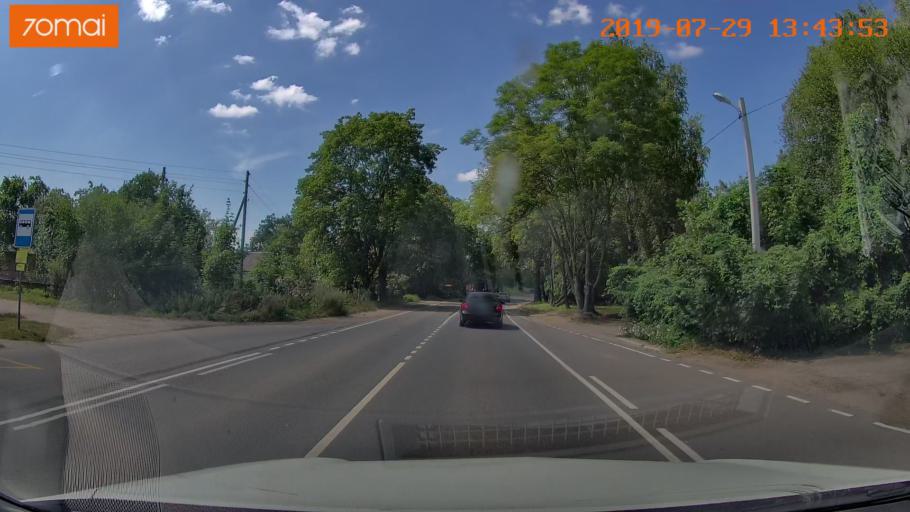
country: RU
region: Kaliningrad
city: Svetlyy
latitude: 54.7371
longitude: 20.0951
